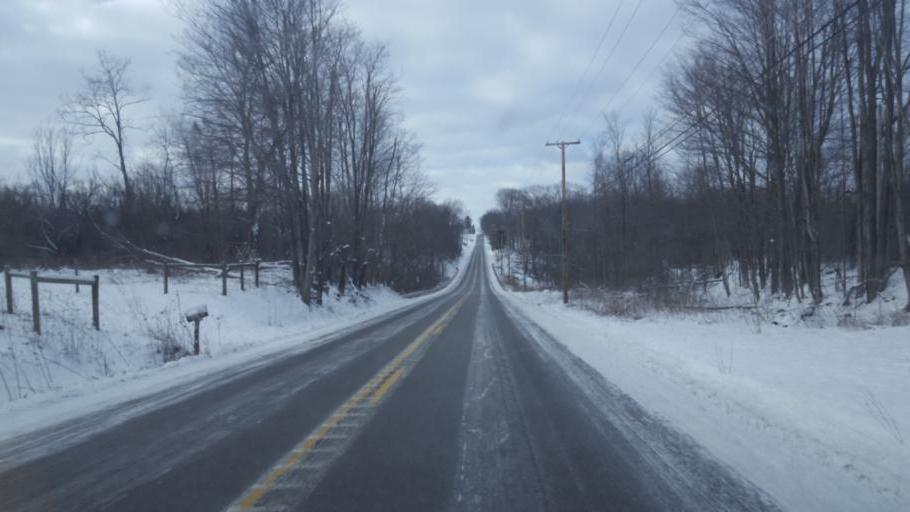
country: US
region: Pennsylvania
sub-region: Mercer County
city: Mercer
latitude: 41.3346
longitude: -80.2284
